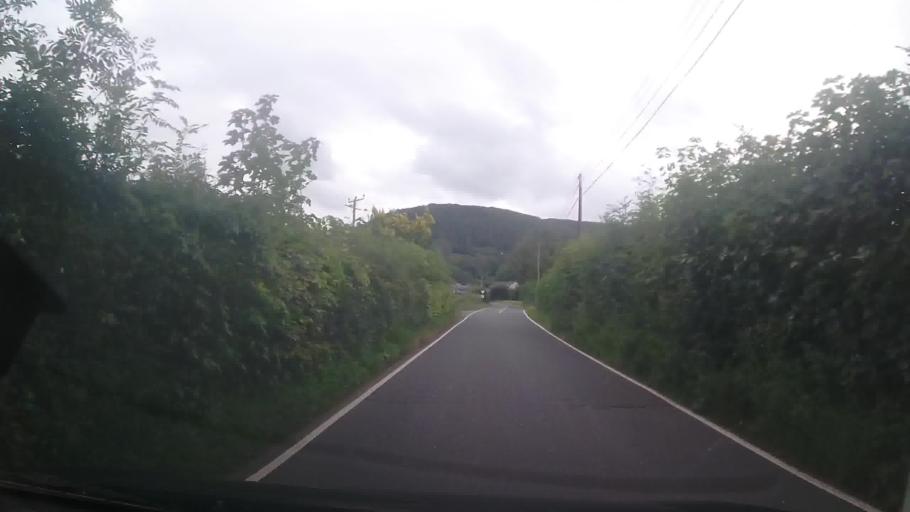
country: GB
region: Wales
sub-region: County of Ceredigion
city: Bow Street
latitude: 52.5138
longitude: -3.9797
